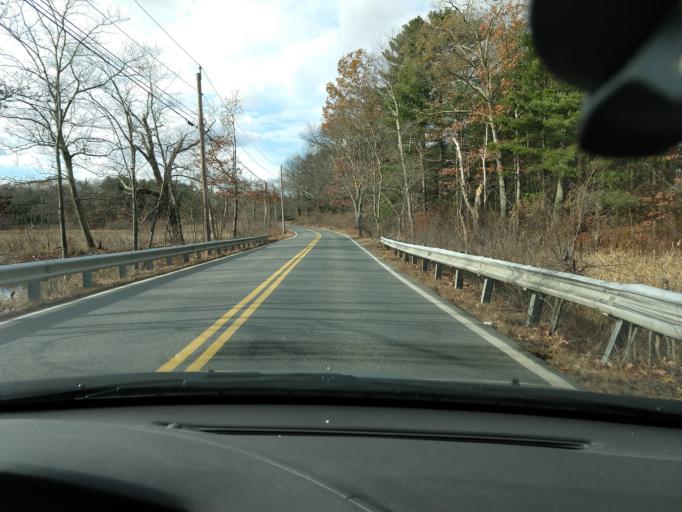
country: US
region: Massachusetts
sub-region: Middlesex County
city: Sudbury
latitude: 42.4097
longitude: -71.3785
